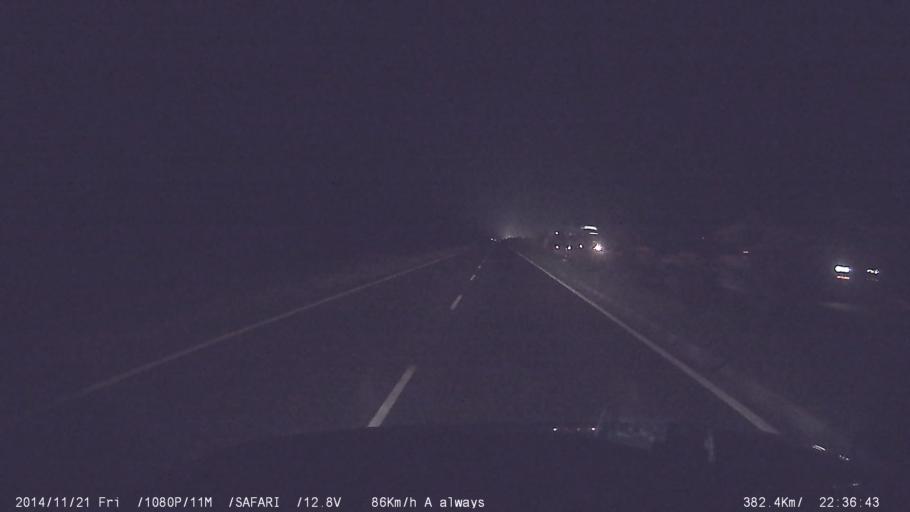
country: IN
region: Tamil Nadu
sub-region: Villupuram
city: Tindivanam
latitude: 12.2849
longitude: 79.7127
